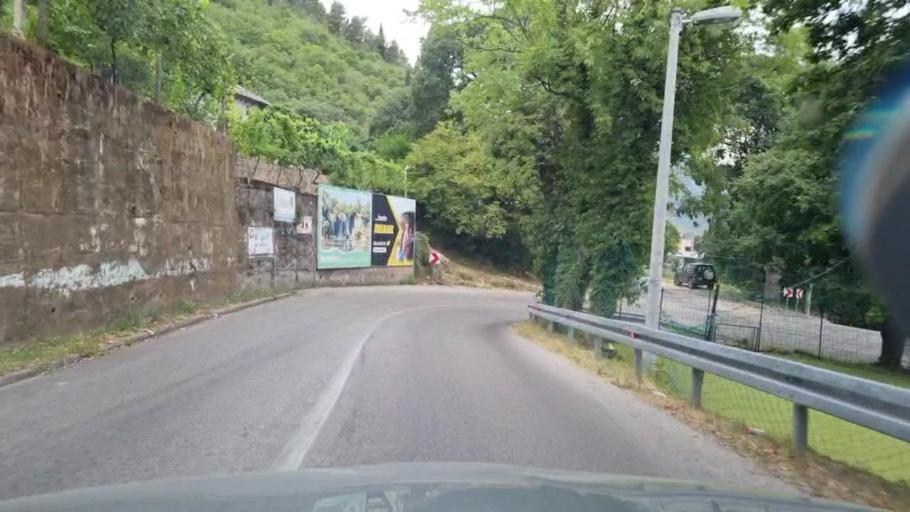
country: BA
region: Federation of Bosnia and Herzegovina
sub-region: Hercegovacko-Bosanski Kanton
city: Mostar
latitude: 43.3311
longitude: 17.7953
